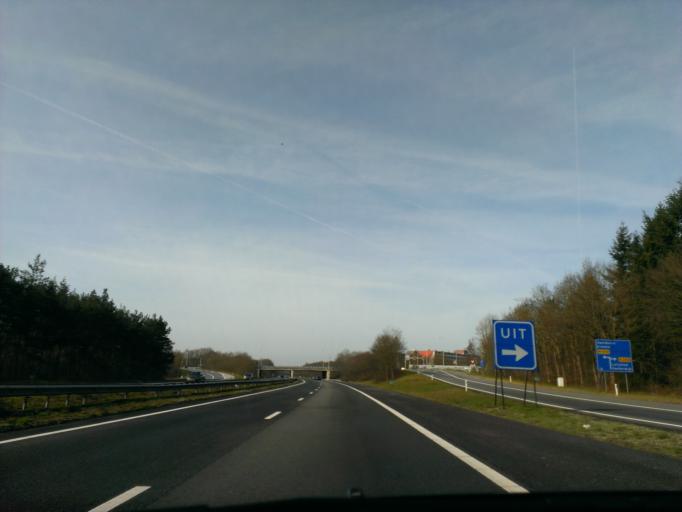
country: NL
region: Gelderland
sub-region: Gemeente Harderwijk
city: Harderwijk
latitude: 52.3393
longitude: 5.6492
